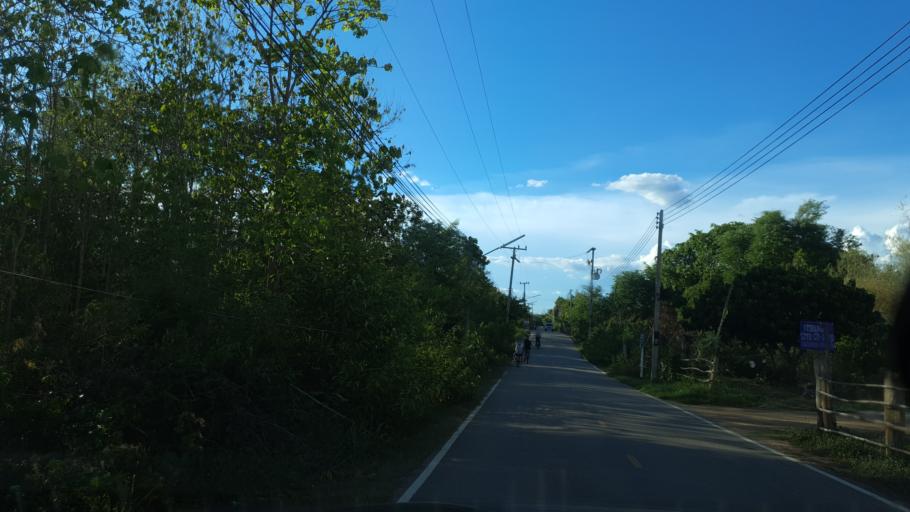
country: TH
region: Lampang
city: Sop Prap
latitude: 17.8874
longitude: 99.3114
